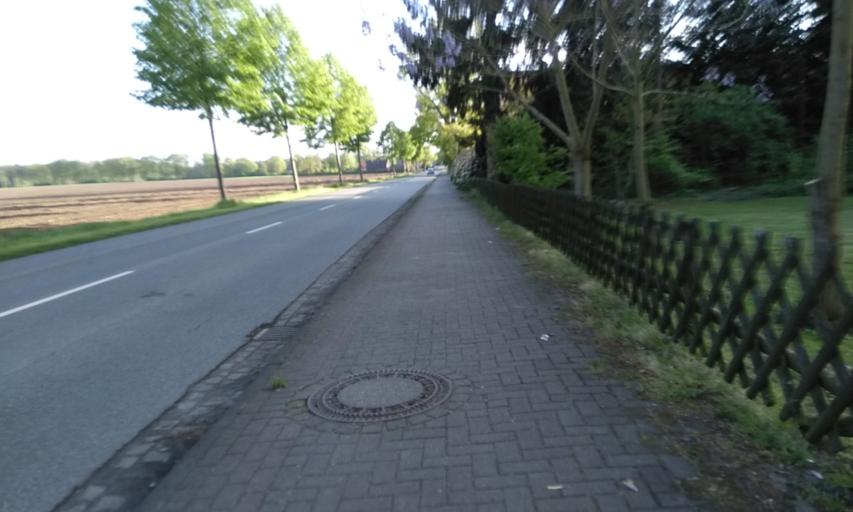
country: DE
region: Lower Saxony
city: Sauensiek
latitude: 53.4109
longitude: 9.5485
